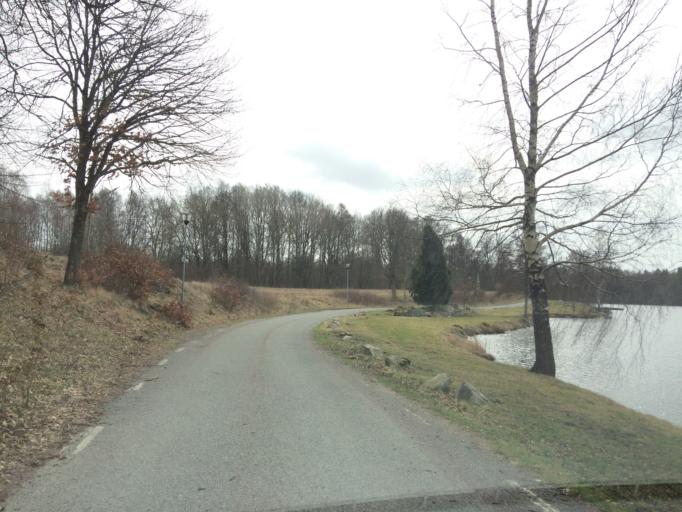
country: SE
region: Skane
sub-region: Ostra Goinge Kommun
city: Sibbhult
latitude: 56.2799
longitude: 14.3036
